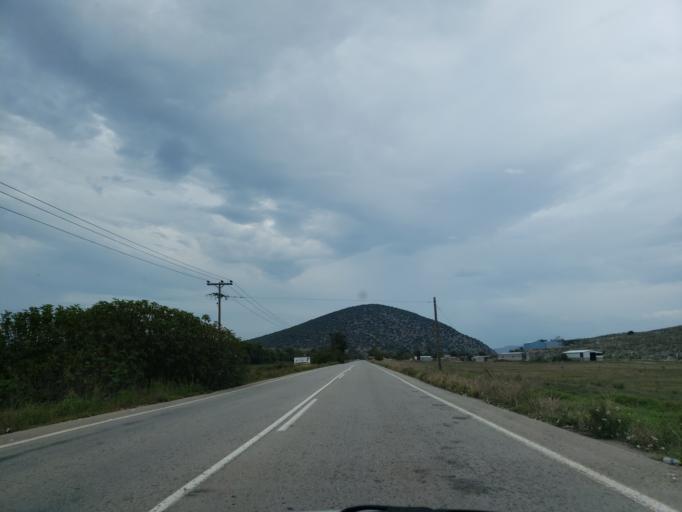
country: GR
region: Central Greece
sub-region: Nomos Voiotias
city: Aliartos
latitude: 38.4795
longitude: 23.0979
